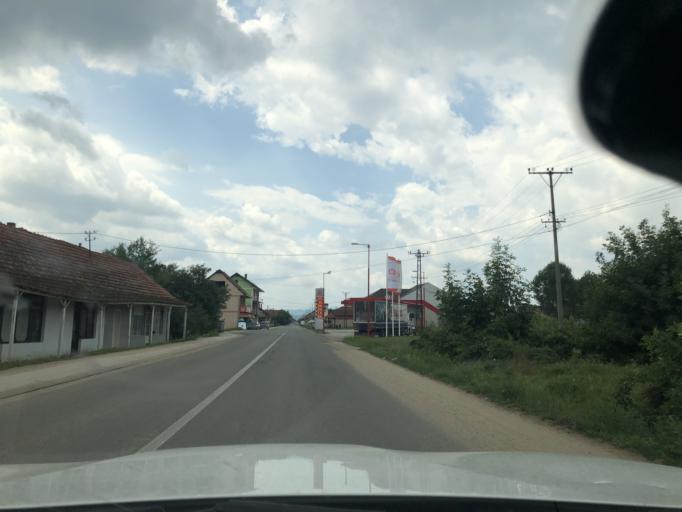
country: RS
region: Central Serbia
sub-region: Jablanicki Okrug
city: Lebane
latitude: 42.9625
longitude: 21.8376
